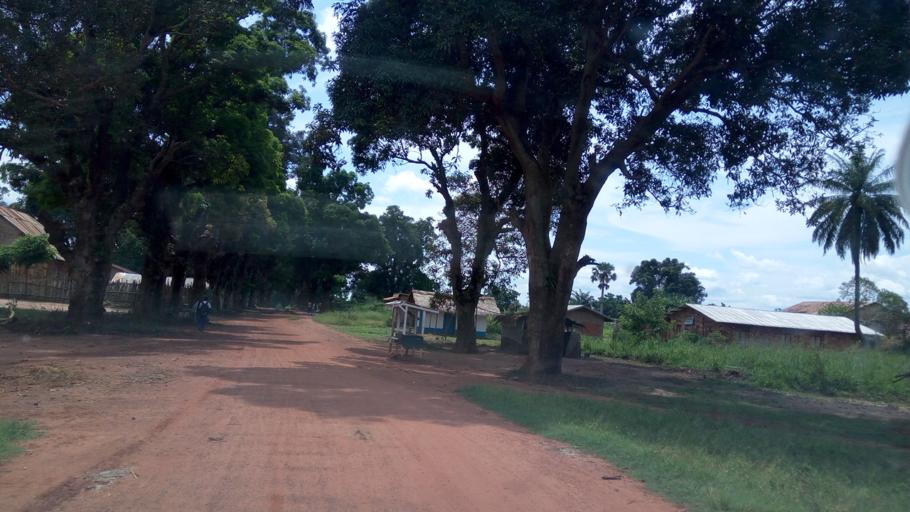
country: CD
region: Equateur
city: Libenge
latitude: 3.6486
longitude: 18.6322
